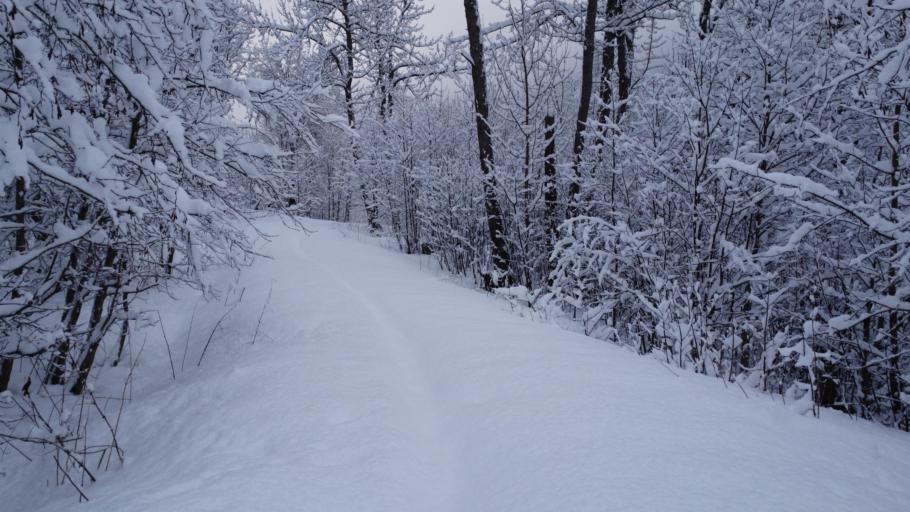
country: NO
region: Nordland
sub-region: Rana
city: Mo i Rana
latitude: 66.3330
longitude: 14.1645
